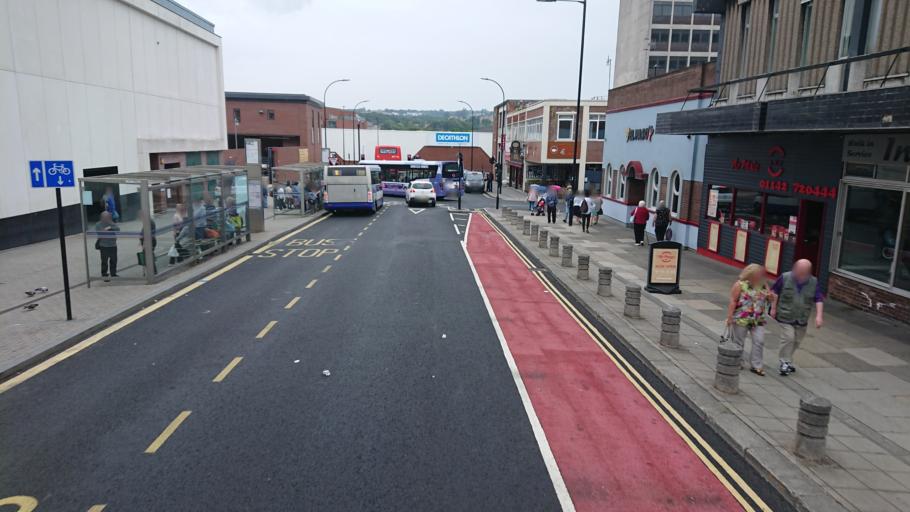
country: GB
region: England
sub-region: Sheffield
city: Sheffield
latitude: 53.3750
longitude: -1.4746
